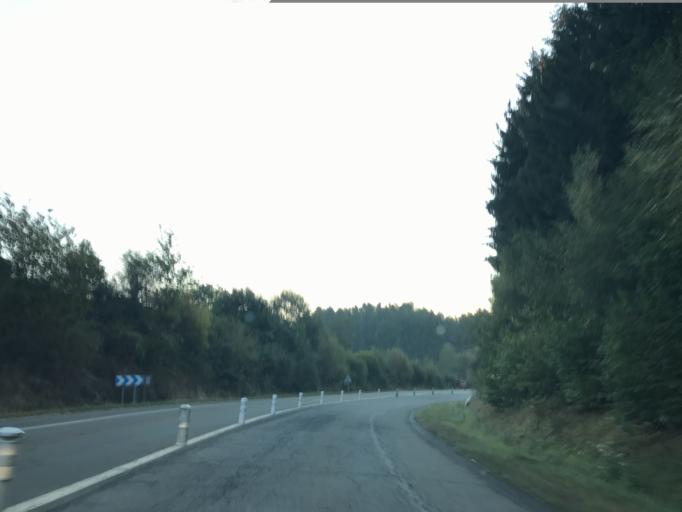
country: FR
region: Auvergne
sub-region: Departement du Puy-de-Dome
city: Celles-sur-Durolle
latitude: 45.8827
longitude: 3.6233
